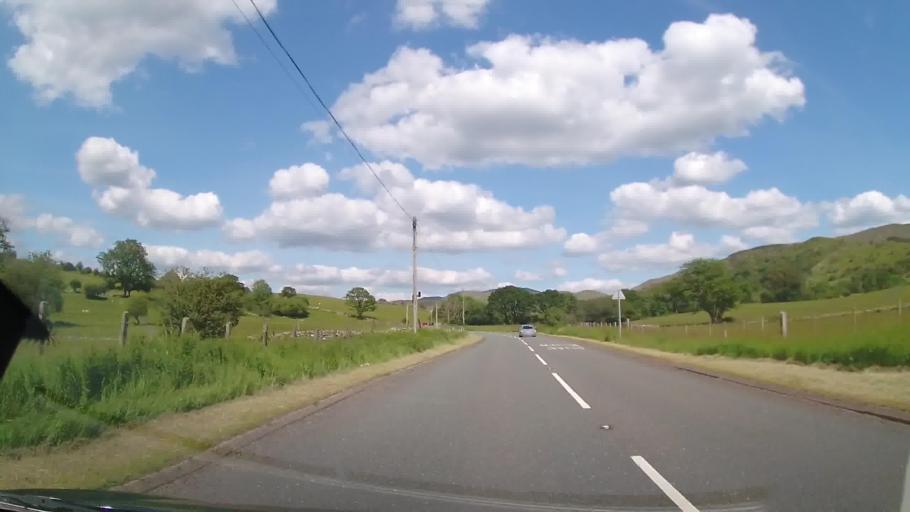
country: GB
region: Wales
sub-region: Gwynedd
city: Dolgellau
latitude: 52.7358
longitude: -3.8202
